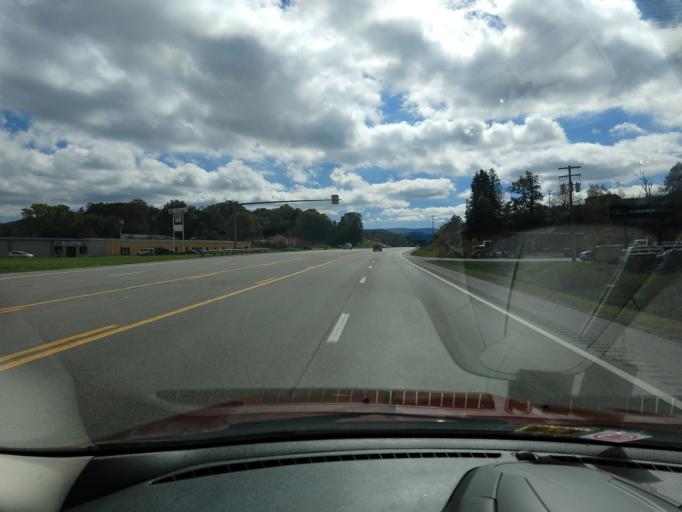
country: US
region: West Virginia
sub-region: Randolph County
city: Elkins
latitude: 38.8862
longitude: -79.8451
